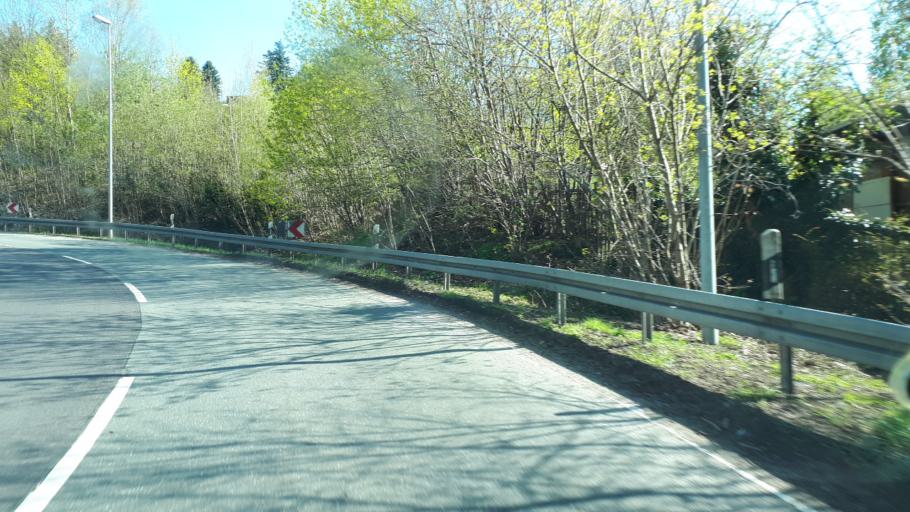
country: DE
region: Saxony
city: Burkhardtsdorf
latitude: 50.7717
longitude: 12.9223
